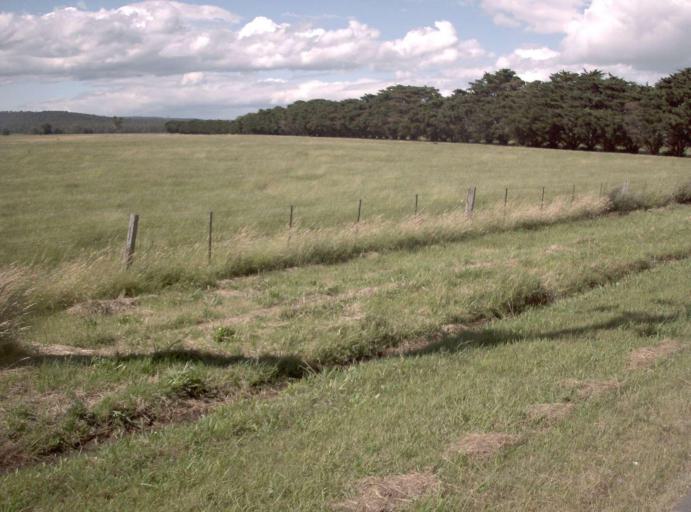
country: AU
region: Victoria
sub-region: Latrobe
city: Traralgon
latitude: -38.1346
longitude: 146.5471
